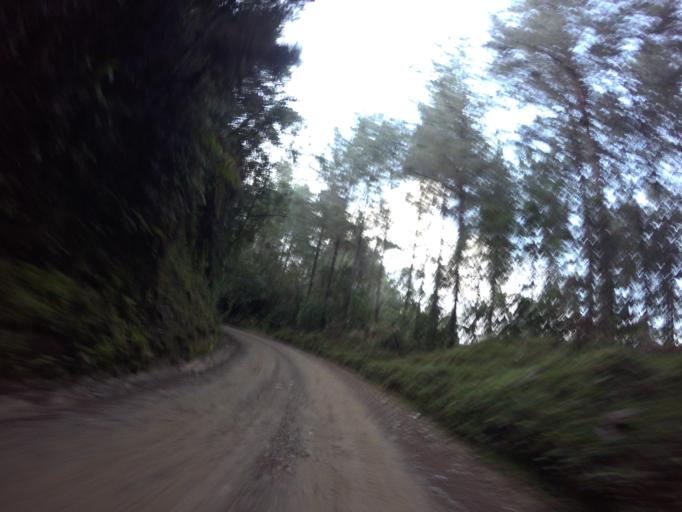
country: CO
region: Caldas
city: Pensilvania
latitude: 5.4475
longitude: -75.1260
